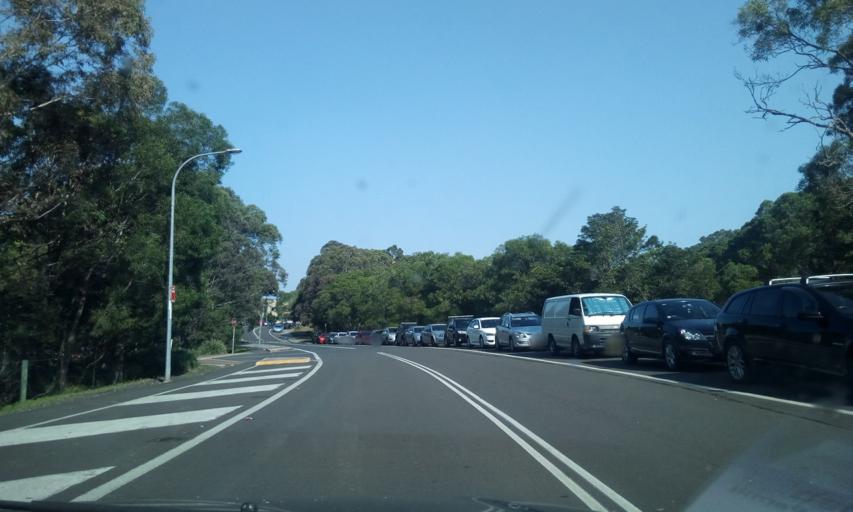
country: AU
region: New South Wales
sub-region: Wollongong
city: Mount Ousley
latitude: -34.4035
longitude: 150.8727
